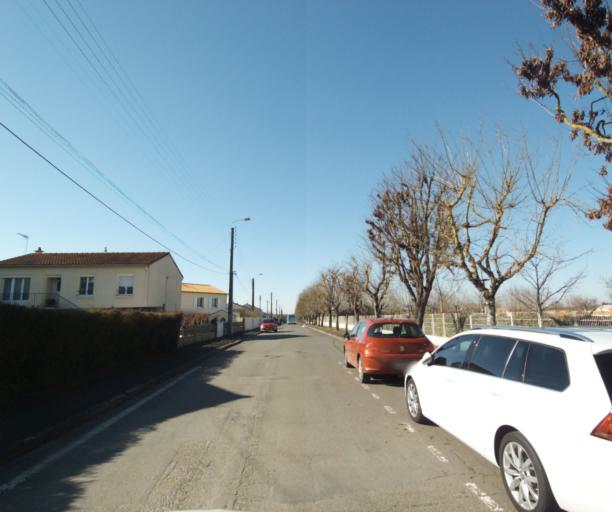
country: FR
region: Poitou-Charentes
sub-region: Departement des Deux-Sevres
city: Niort
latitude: 46.3428
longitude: -0.4820
